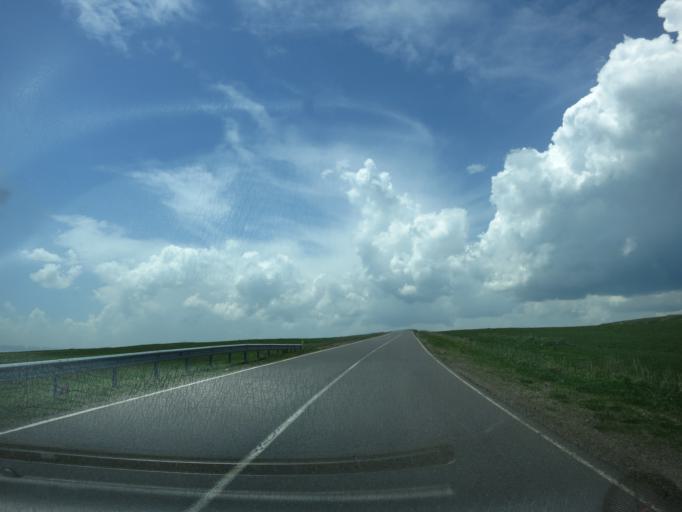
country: GE
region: Samtskhe-Javakheti
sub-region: Ninotsminda
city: Ninotsminda
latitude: 41.2916
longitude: 43.7271
